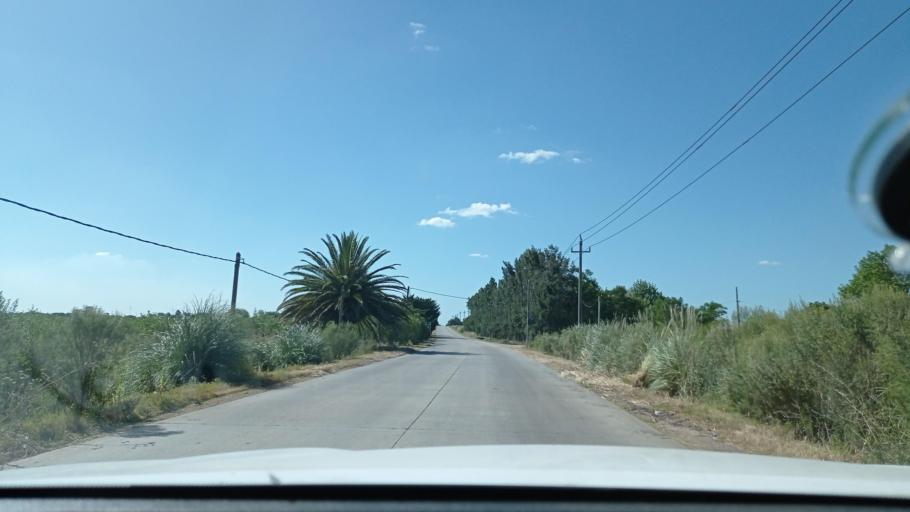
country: UY
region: Canelones
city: La Paz
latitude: -34.7791
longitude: -56.2559
